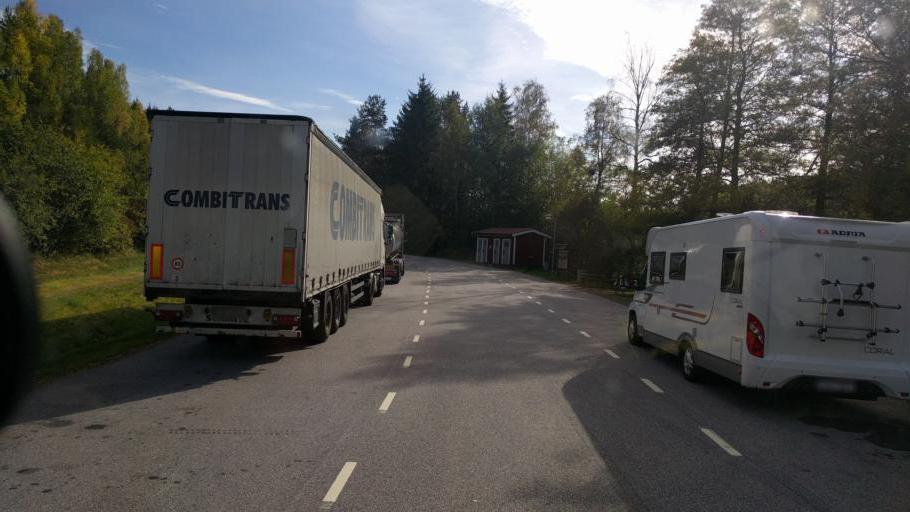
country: SE
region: OEstergoetland
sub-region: Kinda Kommun
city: Kisa
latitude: 57.9340
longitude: 15.6690
